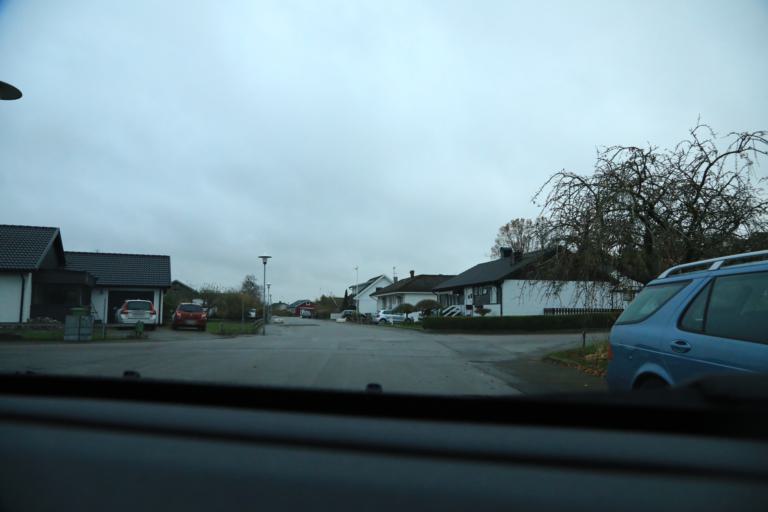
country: SE
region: Halland
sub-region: Varbergs Kommun
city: Varberg
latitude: 57.1743
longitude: 12.2224
